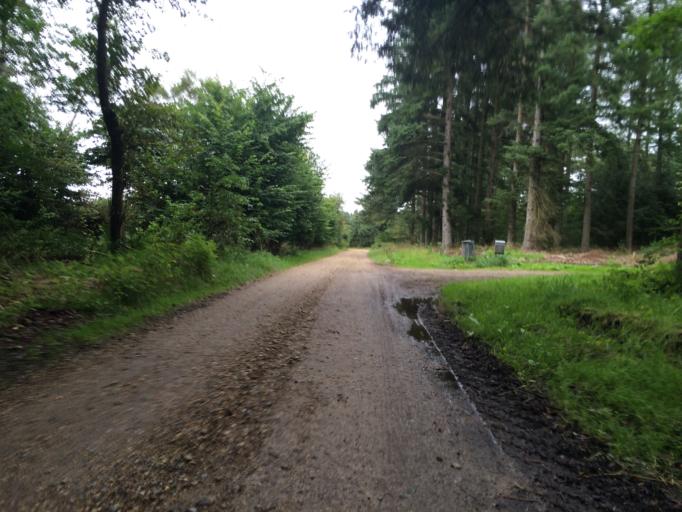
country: DK
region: Central Jutland
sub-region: Holstebro Kommune
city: Ulfborg
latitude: 56.2237
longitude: 8.4079
